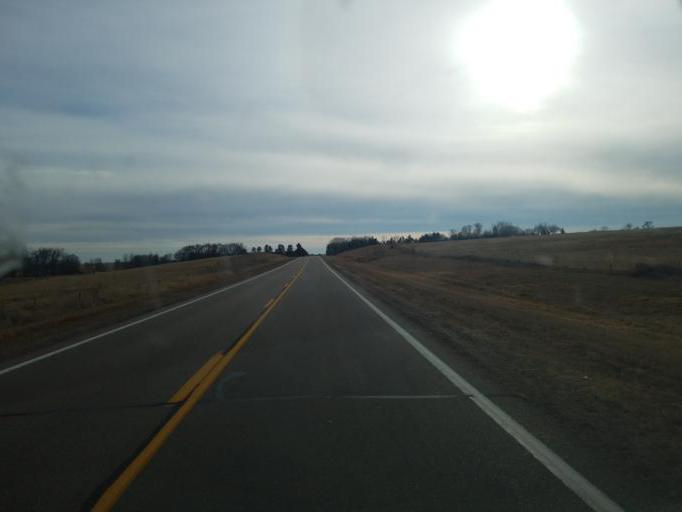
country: US
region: Nebraska
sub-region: Knox County
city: Creighton
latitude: 42.4502
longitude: -97.8967
